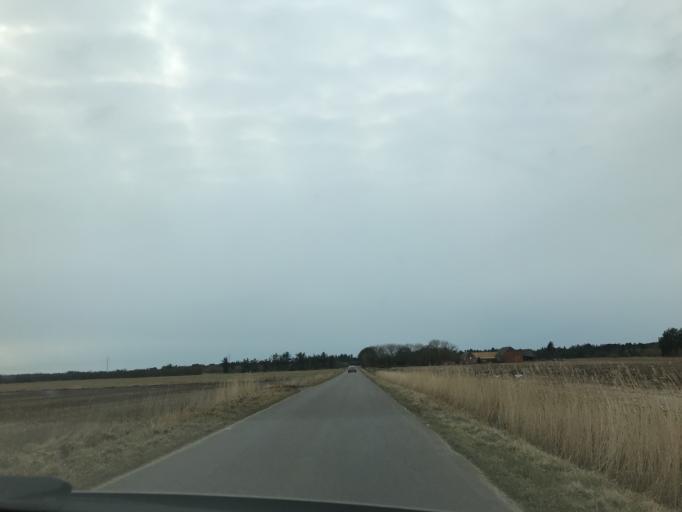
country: DK
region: South Denmark
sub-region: Varde Kommune
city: Oksbol
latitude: 55.8180
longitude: 8.2419
